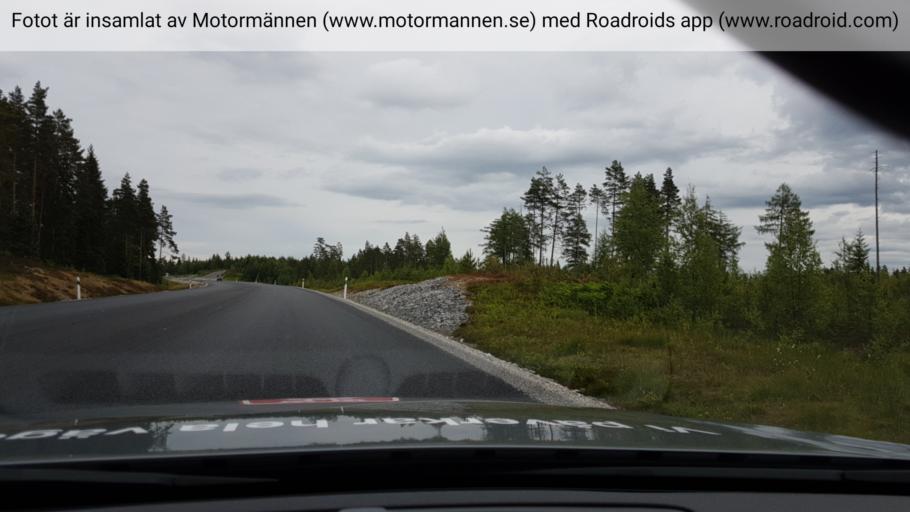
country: SE
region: Vaestmanland
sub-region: Skinnskattebergs Kommun
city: Skinnskatteberg
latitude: 59.8458
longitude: 15.5802
